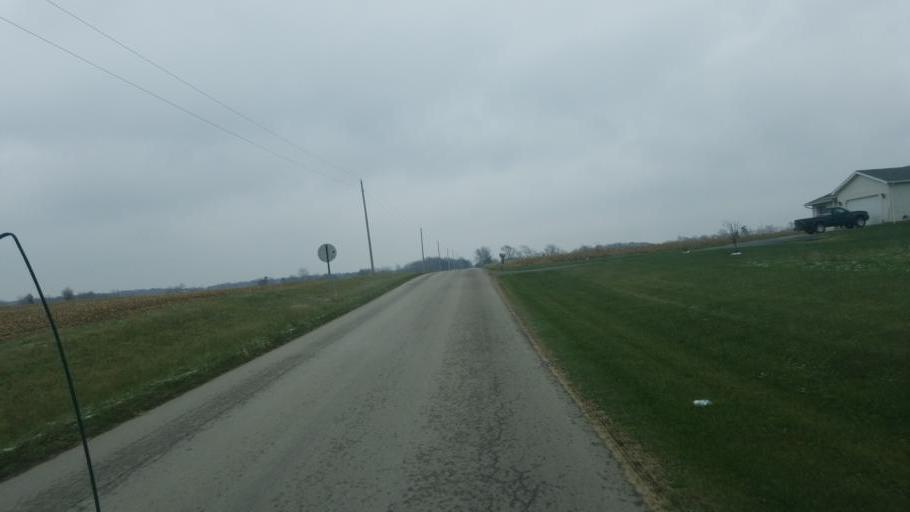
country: US
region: Ohio
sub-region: Lorain County
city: Wellington
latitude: 41.0850
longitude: -82.2316
